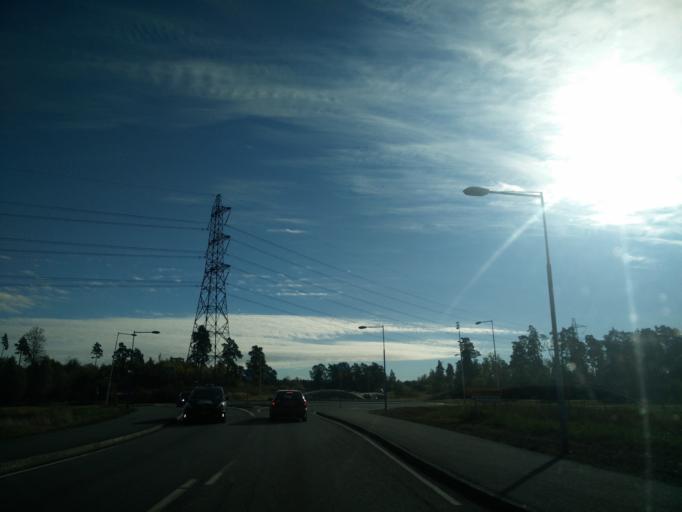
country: SE
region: Stockholm
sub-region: Upplands Vasby Kommun
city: Upplands Vaesby
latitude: 59.5062
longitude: 17.9713
